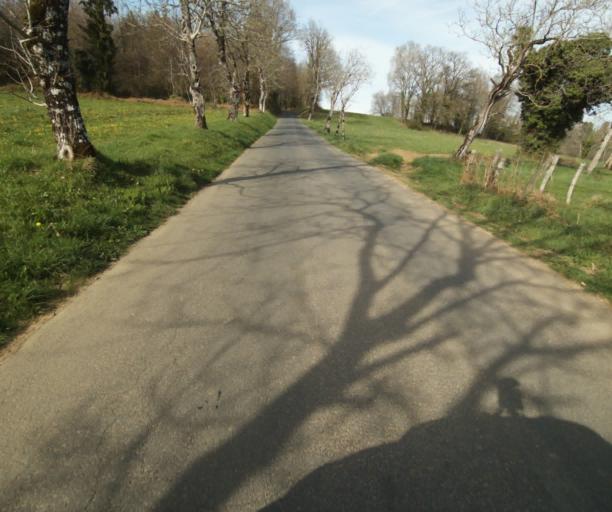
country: FR
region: Limousin
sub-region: Departement de la Correze
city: Naves
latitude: 45.3309
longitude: 1.7563
